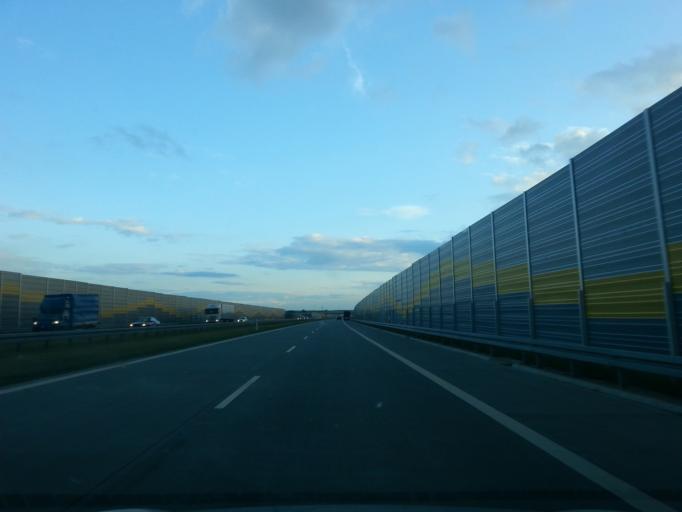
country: PL
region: Lodz Voivodeship
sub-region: Powiat sieradzki
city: Brzeznio
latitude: 51.4934
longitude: 18.6836
